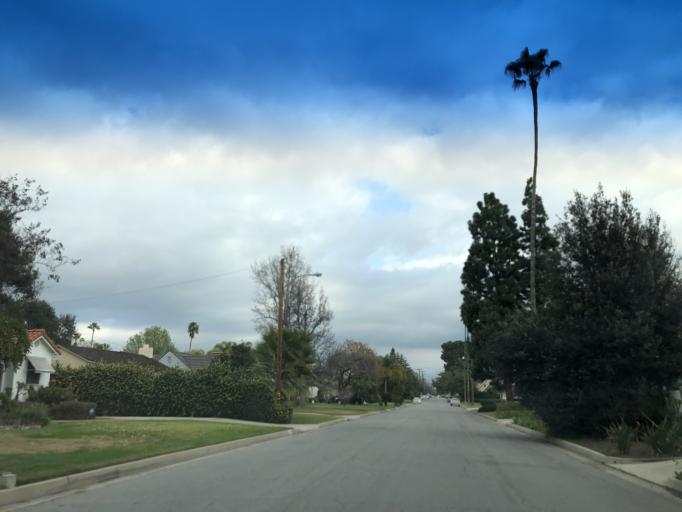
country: US
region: California
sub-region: Los Angeles County
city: San Marino
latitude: 34.1171
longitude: -118.0938
